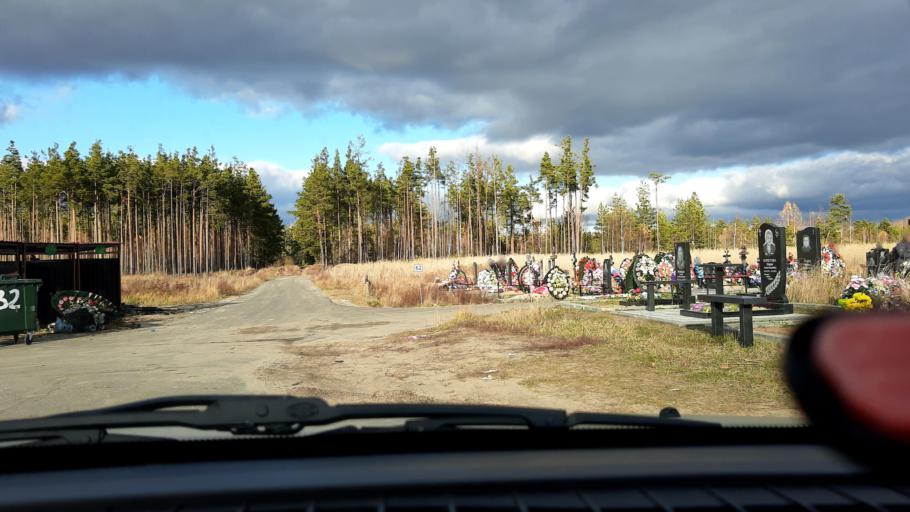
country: RU
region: Nizjnij Novgorod
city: Gorbatovka
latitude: 56.3623
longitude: 43.7710
